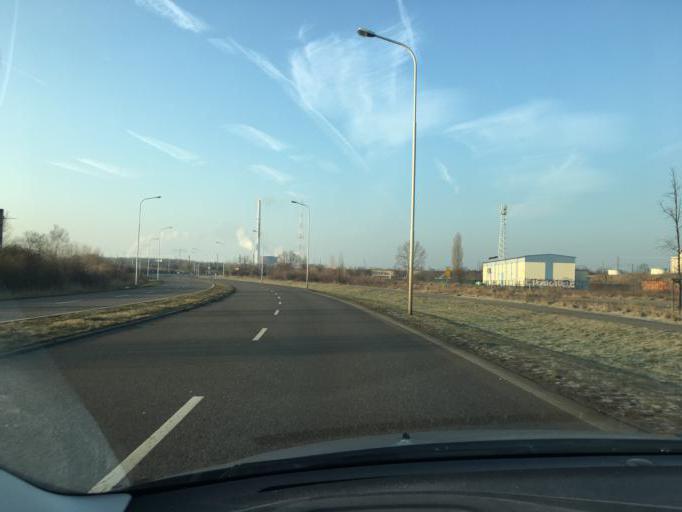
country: DE
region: Saxony-Anhalt
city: Halle (Saale)
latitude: 51.4693
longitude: 12.0056
